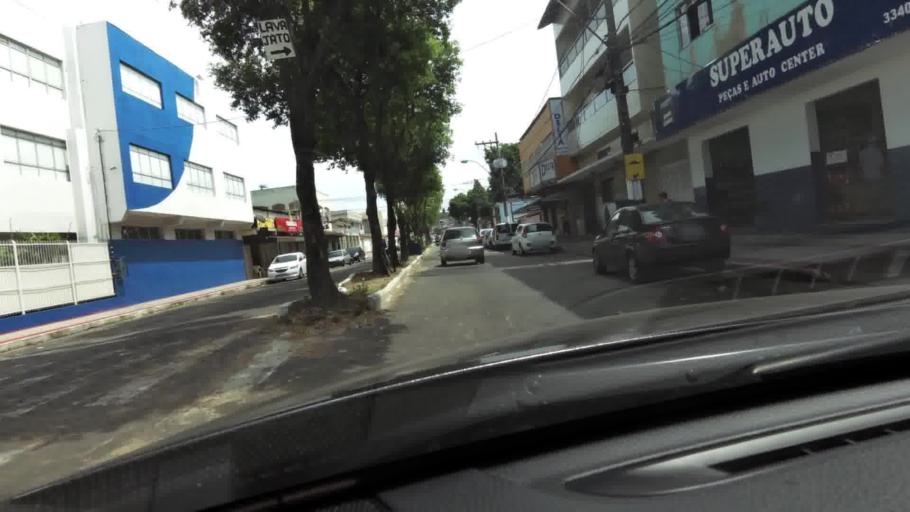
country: BR
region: Espirito Santo
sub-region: Vila Velha
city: Vila Velha
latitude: -20.3403
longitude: -40.3057
